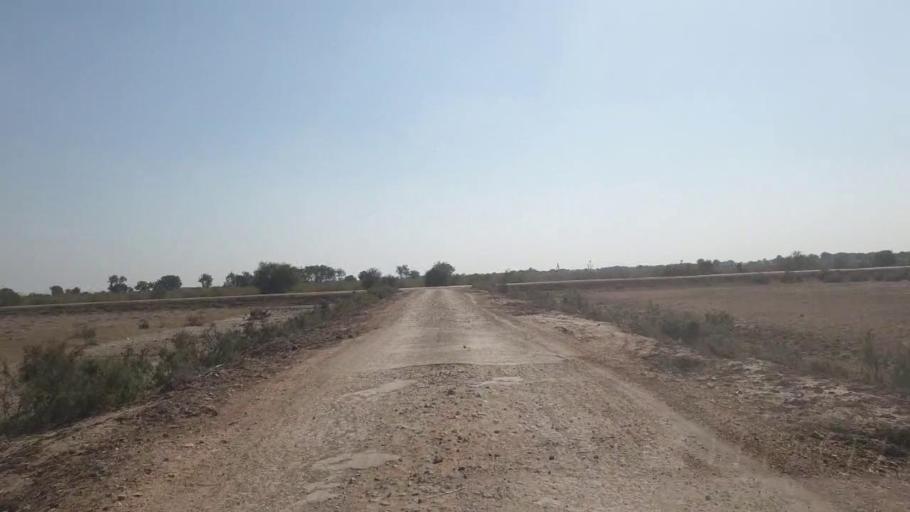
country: PK
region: Sindh
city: Chambar
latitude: 25.2953
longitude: 68.7418
